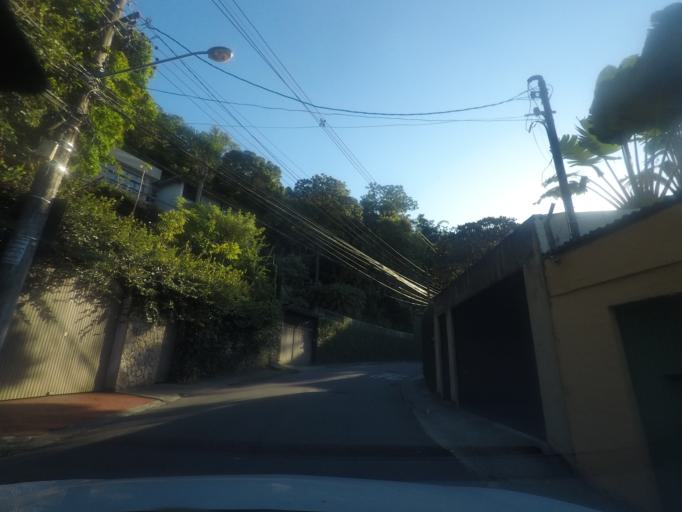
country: BR
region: Rio de Janeiro
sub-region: Rio De Janeiro
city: Rio de Janeiro
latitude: -22.9361
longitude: -43.1983
